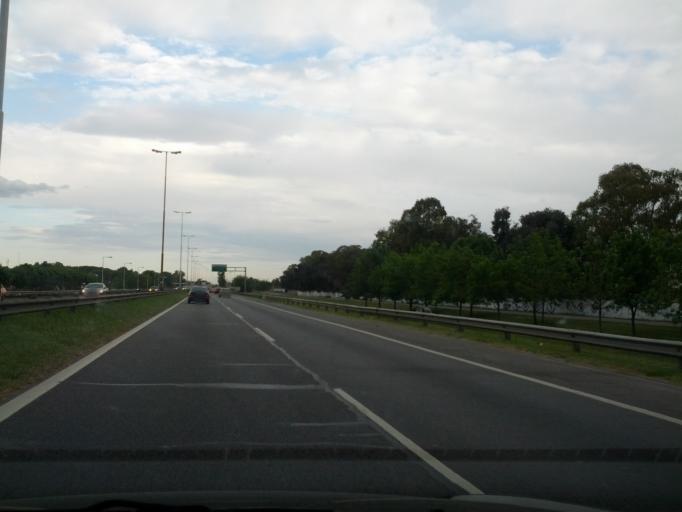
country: AR
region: Buenos Aires
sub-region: Partido de General Rodriguez
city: General Rodriguez
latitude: -34.5915
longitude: -58.9555
